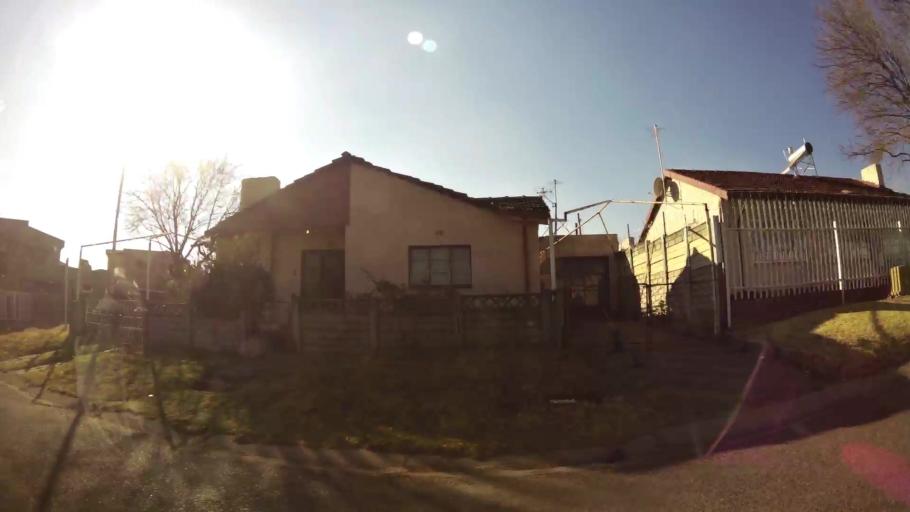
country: ZA
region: Gauteng
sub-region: City of Johannesburg Metropolitan Municipality
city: Roodepoort
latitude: -26.1616
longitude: 27.8593
